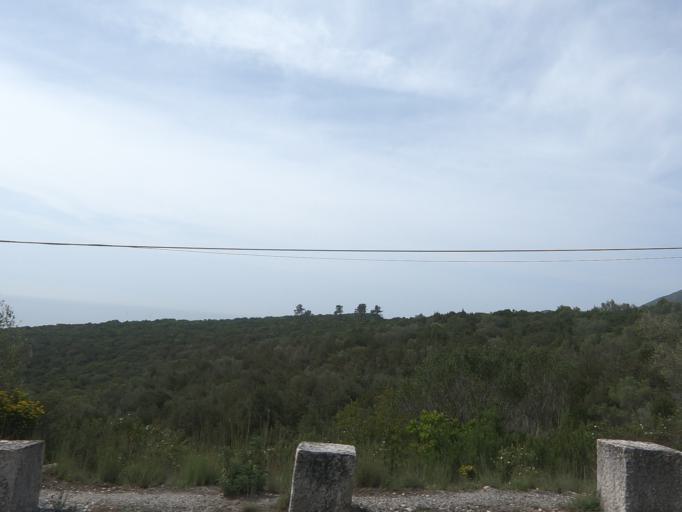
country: PT
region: Setubal
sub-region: Palmela
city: Quinta do Anjo
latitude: 38.4848
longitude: -8.9719
